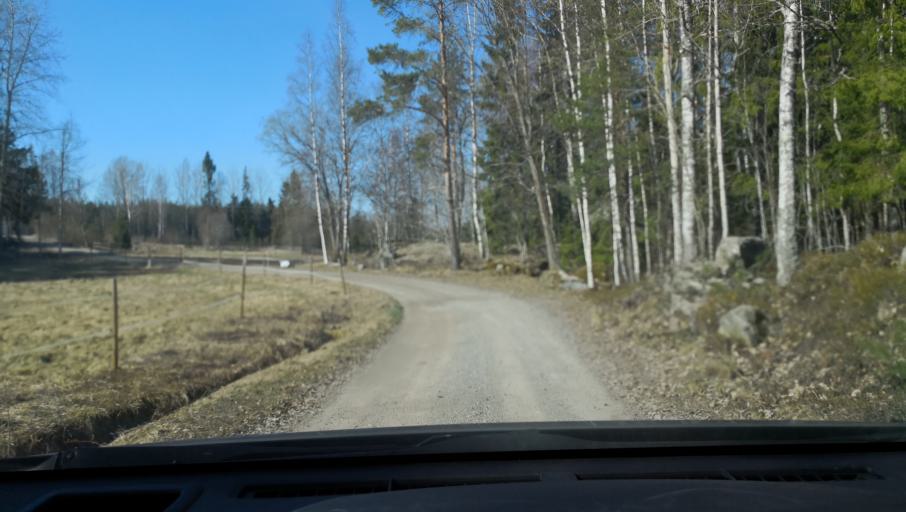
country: SE
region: Vaestmanland
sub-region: Sala Kommun
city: Sala
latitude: 59.9440
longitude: 16.4385
